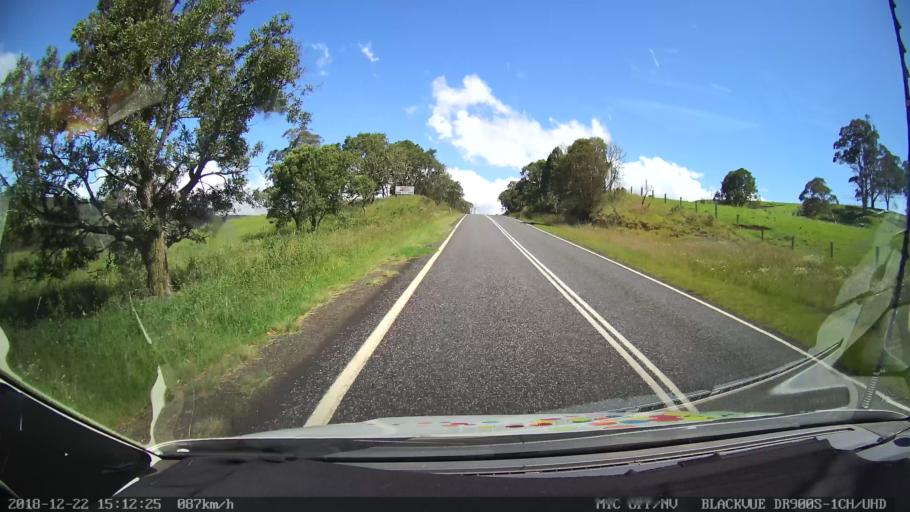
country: AU
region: New South Wales
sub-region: Bellingen
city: Dorrigo
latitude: -30.3555
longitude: 152.3972
